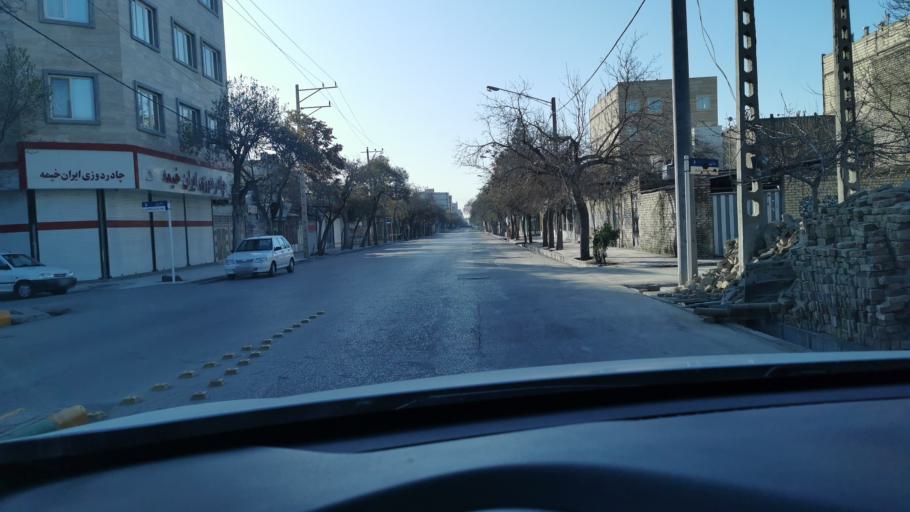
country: IR
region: Razavi Khorasan
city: Mashhad
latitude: 36.3016
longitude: 59.6334
